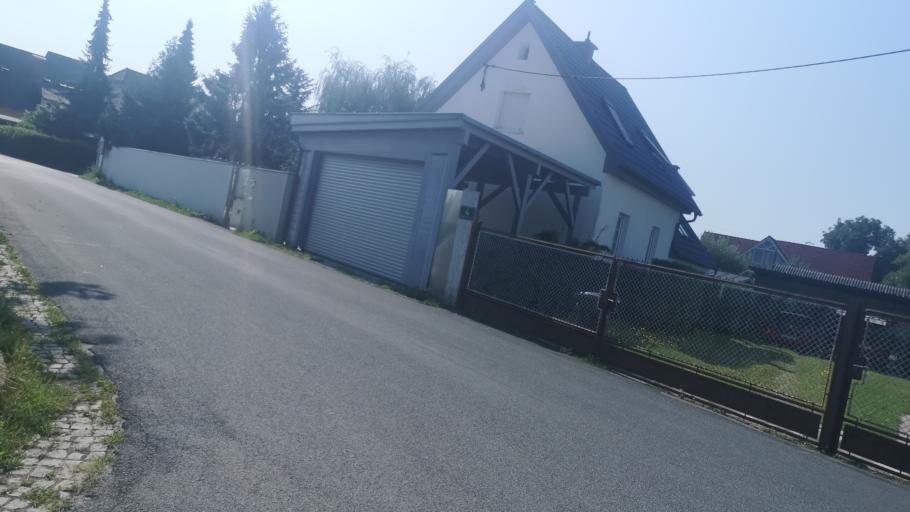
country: AT
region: Styria
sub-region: Graz Stadt
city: Wetzelsdorf
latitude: 47.0306
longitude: 15.4070
